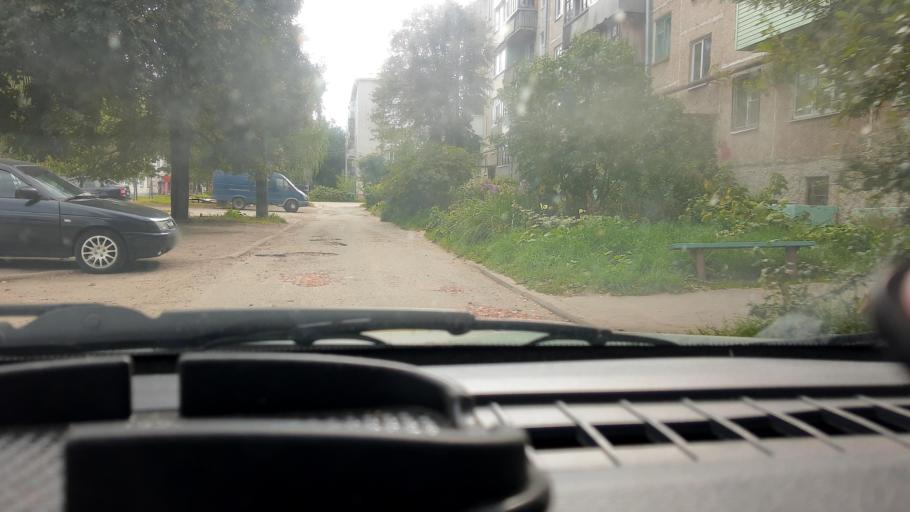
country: RU
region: Mariy-El
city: Medvedevo
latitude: 56.6374
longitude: 47.7967
